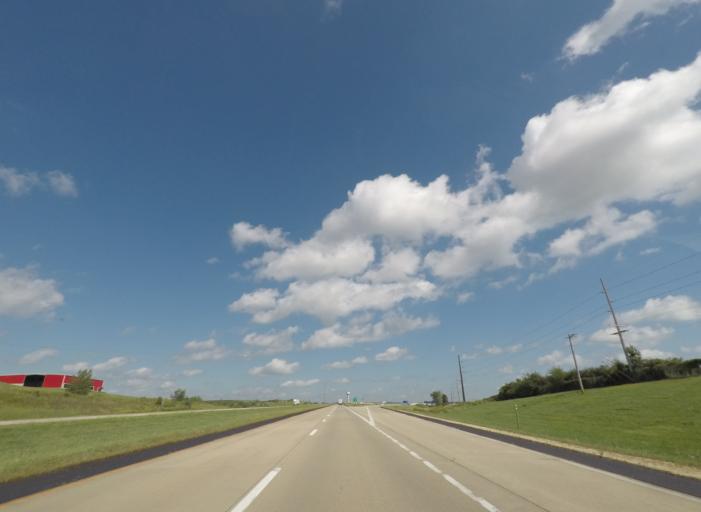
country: US
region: Iowa
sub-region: Dubuque County
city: Cascade
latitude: 42.3106
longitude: -91.0044
